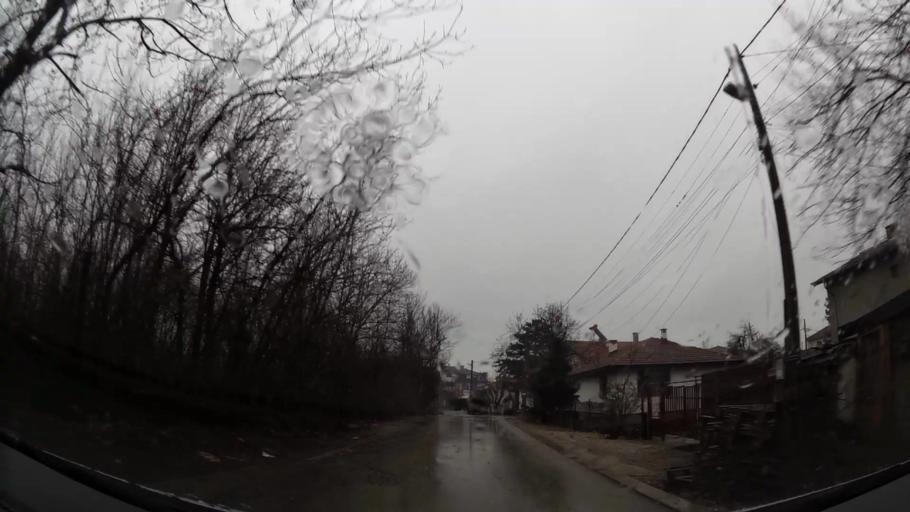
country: BG
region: Sofia-Capital
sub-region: Stolichna Obshtina
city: Sofia
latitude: 42.6291
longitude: 23.3661
